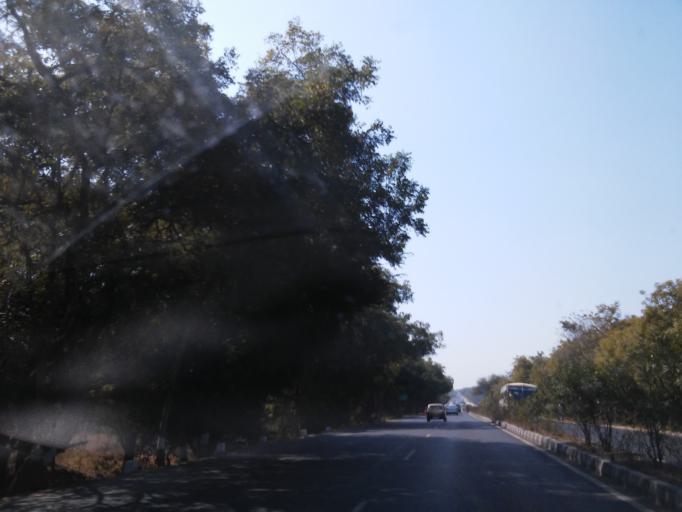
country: IN
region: Gujarat
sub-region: Gandhinagar
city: Ghandinagar
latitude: 23.2467
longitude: 72.6906
